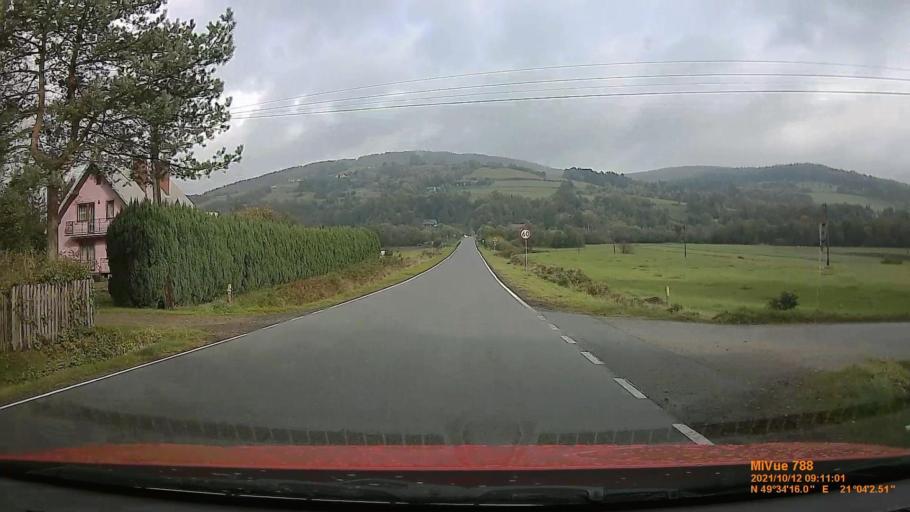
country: PL
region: Lesser Poland Voivodeship
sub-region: Powiat gorlicki
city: Ropa
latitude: 49.5713
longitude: 21.0674
